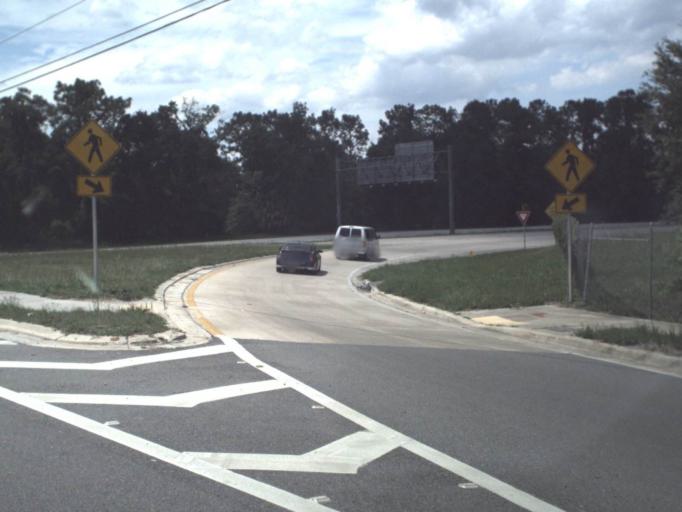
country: US
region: Florida
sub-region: Saint Johns County
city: Fruit Cove
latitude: 30.1681
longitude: -81.5411
